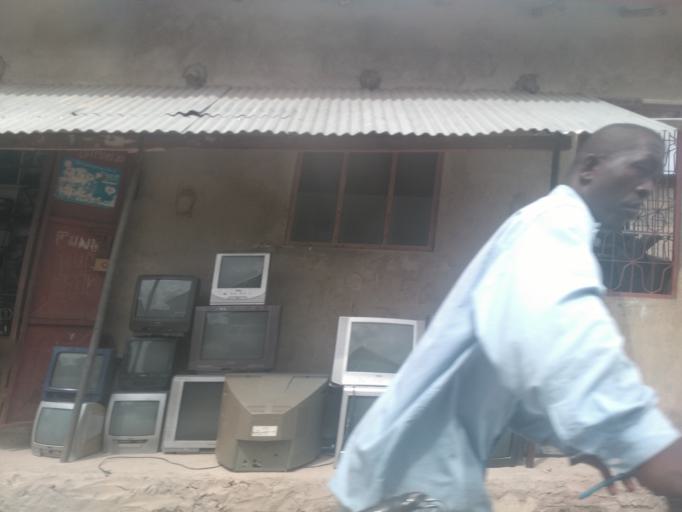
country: TZ
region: Zanzibar Urban/West
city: Zanzibar
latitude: -6.1747
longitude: 39.2401
